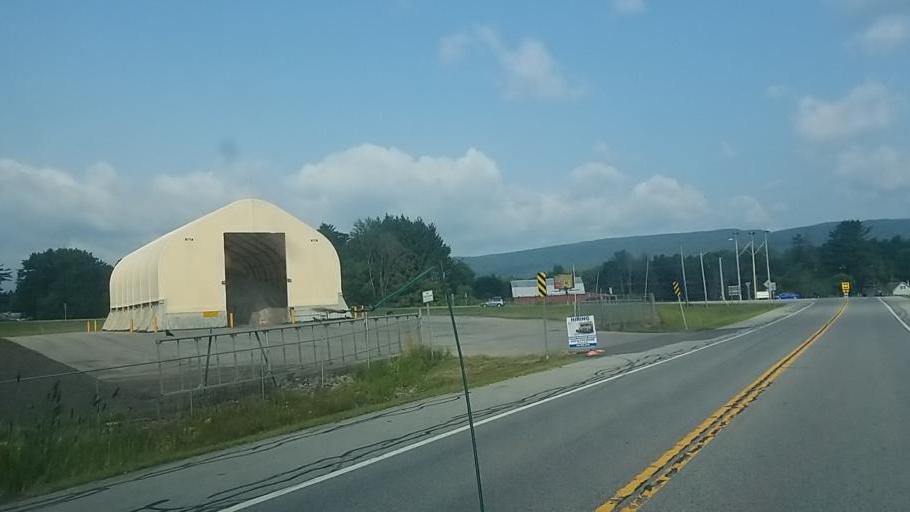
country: US
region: New York
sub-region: Fulton County
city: Gloversville
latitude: 43.0937
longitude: -74.2780
